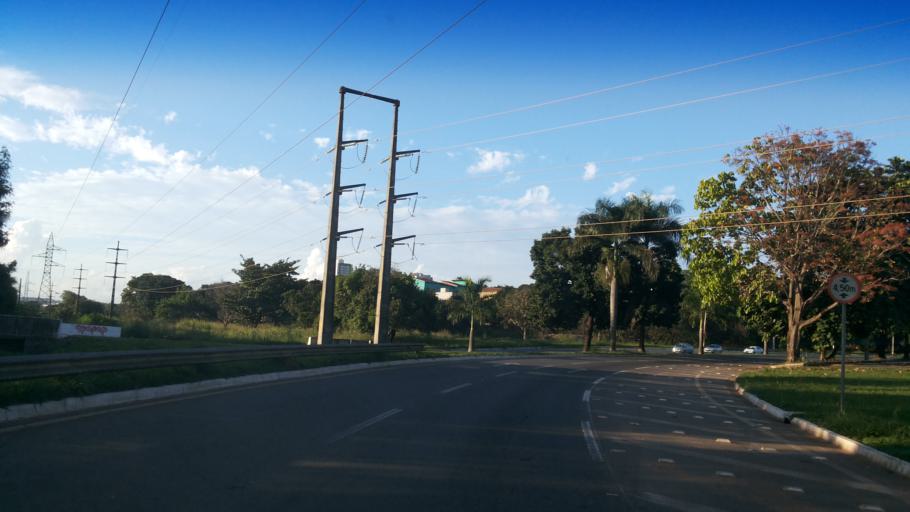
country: BR
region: Goias
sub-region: Goiania
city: Goiania
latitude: -16.6540
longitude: -49.2626
